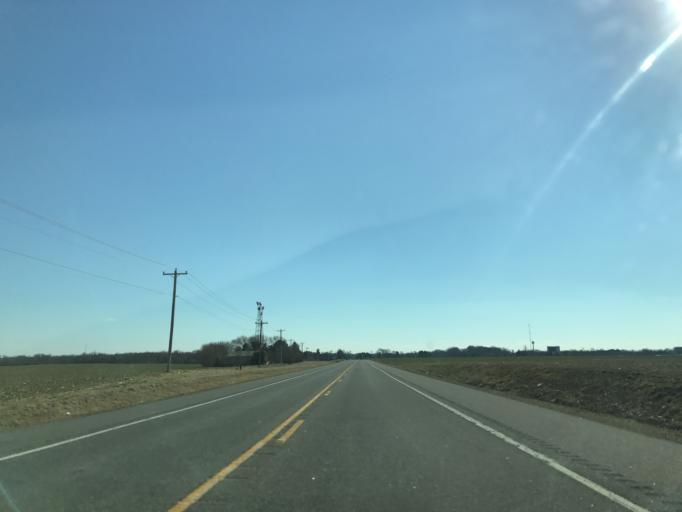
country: US
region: Maryland
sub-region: Queen Anne's County
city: Centreville
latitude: 38.9640
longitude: -76.0778
